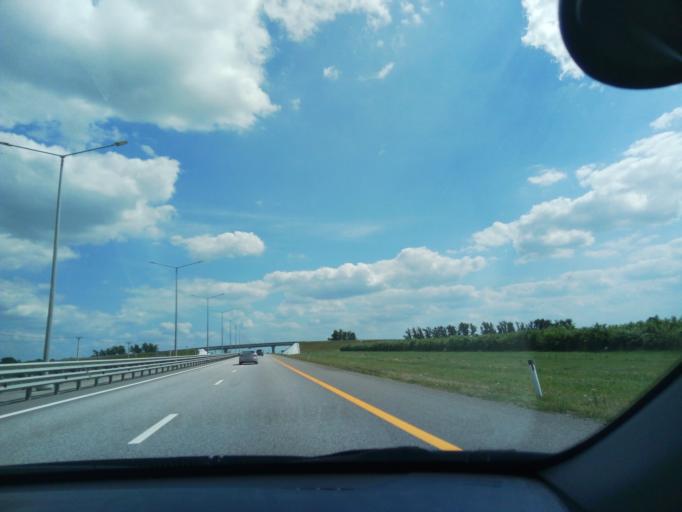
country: RU
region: Voronezj
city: Podkletnoye
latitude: 51.5726
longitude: 39.4704
